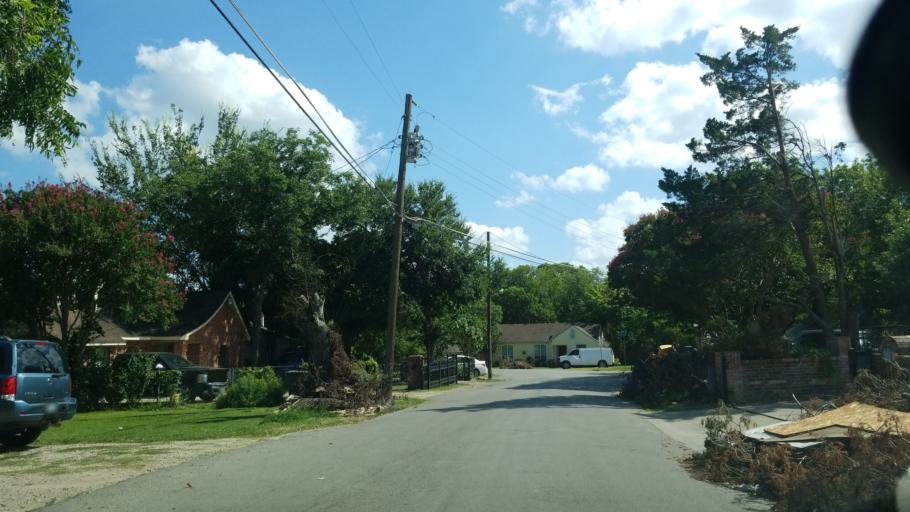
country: US
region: Texas
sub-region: Dallas County
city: Balch Springs
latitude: 32.7698
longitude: -96.6977
